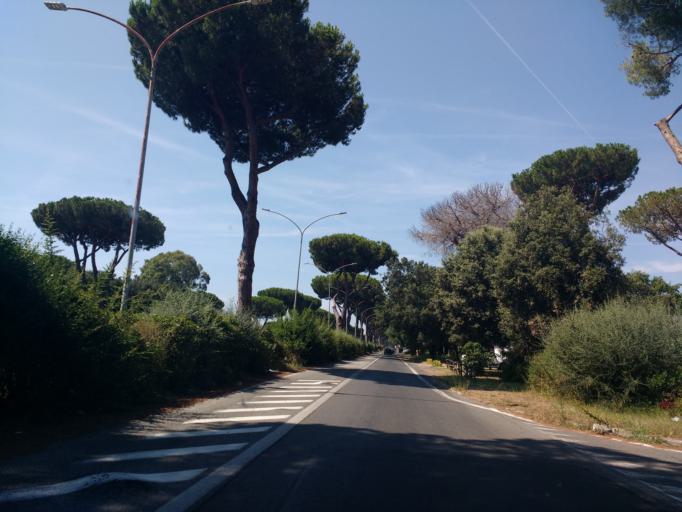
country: IT
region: Latium
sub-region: Citta metropolitana di Roma Capitale
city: Acilia-Castel Fusano-Ostia Antica
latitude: 41.7426
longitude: 12.3535
